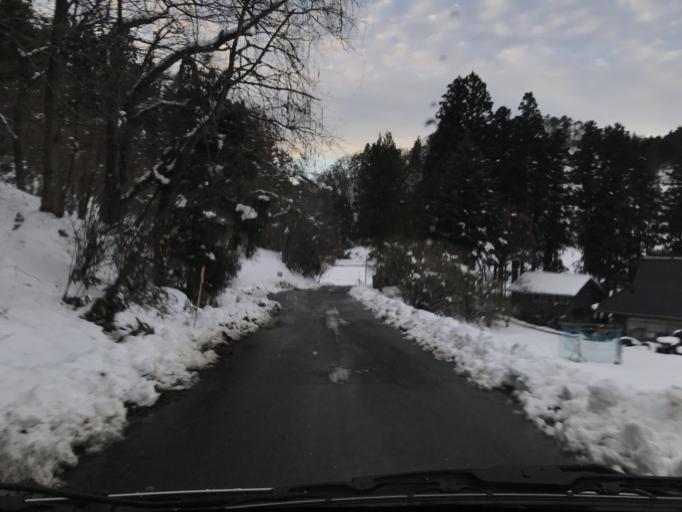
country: JP
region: Iwate
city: Mizusawa
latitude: 39.0463
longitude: 141.0187
